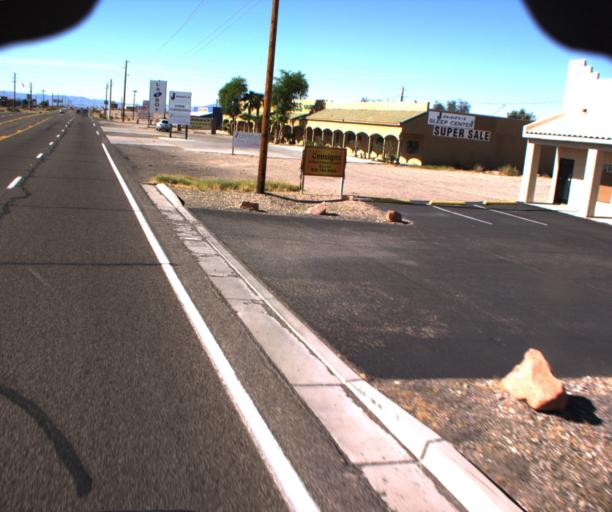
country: US
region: Arizona
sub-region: Mohave County
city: Mohave Valley
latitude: 34.9917
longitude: -114.5981
